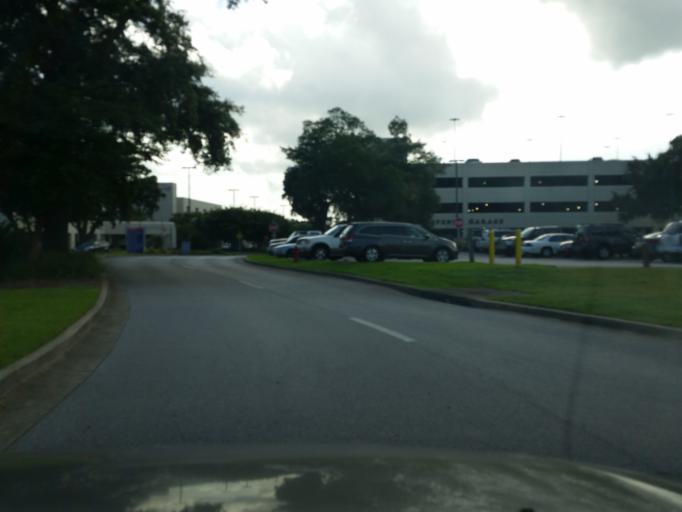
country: US
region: Florida
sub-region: Escambia County
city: Brent
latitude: 30.4776
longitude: -87.2102
